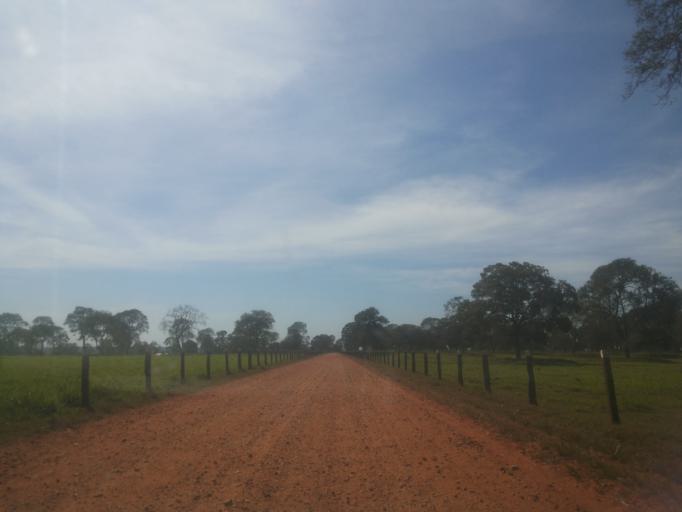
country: BR
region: Minas Gerais
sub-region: Santa Vitoria
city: Santa Vitoria
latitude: -19.0132
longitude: -50.4314
